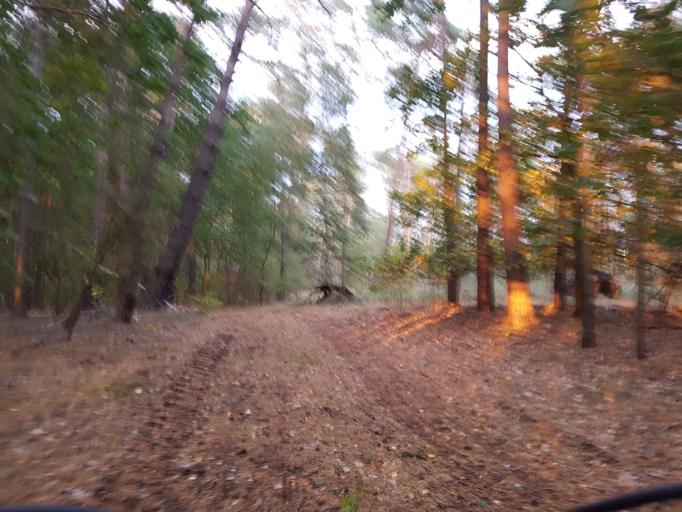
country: DE
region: Brandenburg
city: Schilda
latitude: 51.5980
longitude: 13.3646
